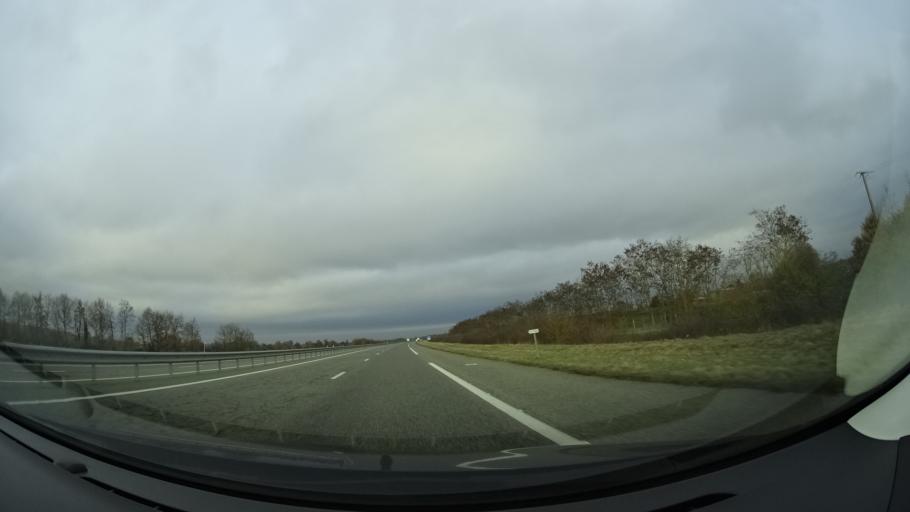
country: FR
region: Midi-Pyrenees
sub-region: Departement de l'Ariege
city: Pamiers
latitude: 43.1637
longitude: 1.6168
